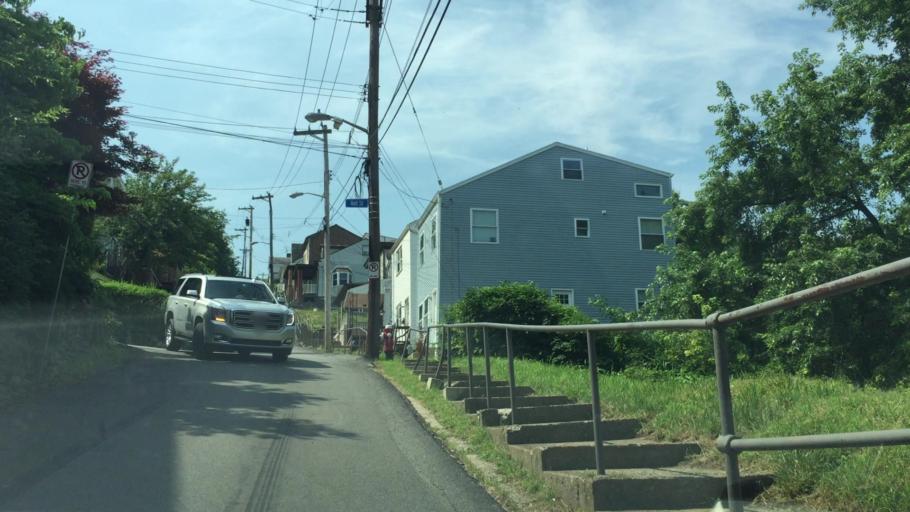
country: US
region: Pennsylvania
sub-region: Allegheny County
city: Mount Oliver
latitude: 40.4225
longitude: -79.9739
